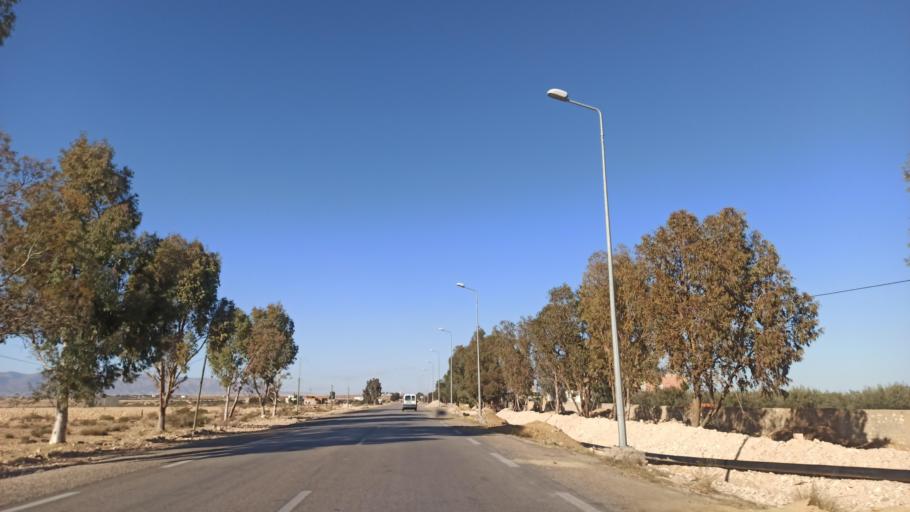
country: TN
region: Sidi Bu Zayd
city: Jilma
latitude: 35.2930
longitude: 9.4169
